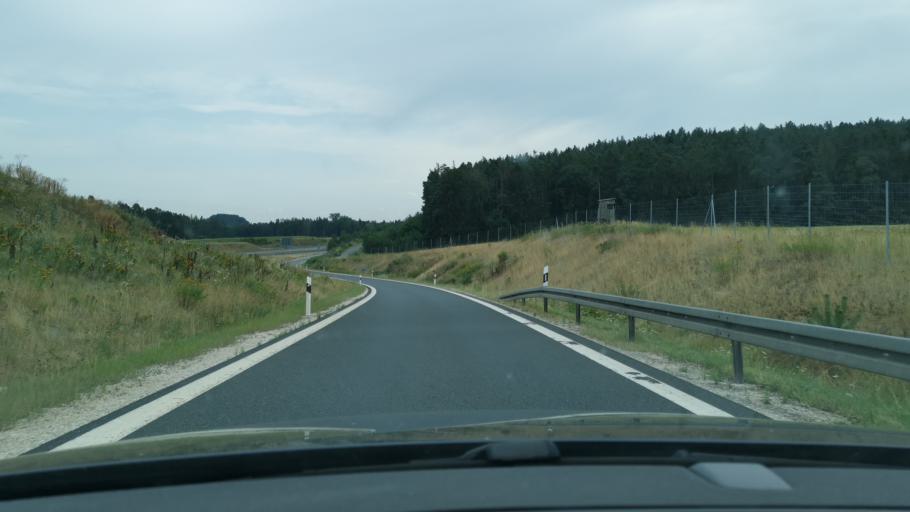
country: DE
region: Bavaria
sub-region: Upper Palatinate
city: Wernberg-Koblitz
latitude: 49.5194
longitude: 12.1611
